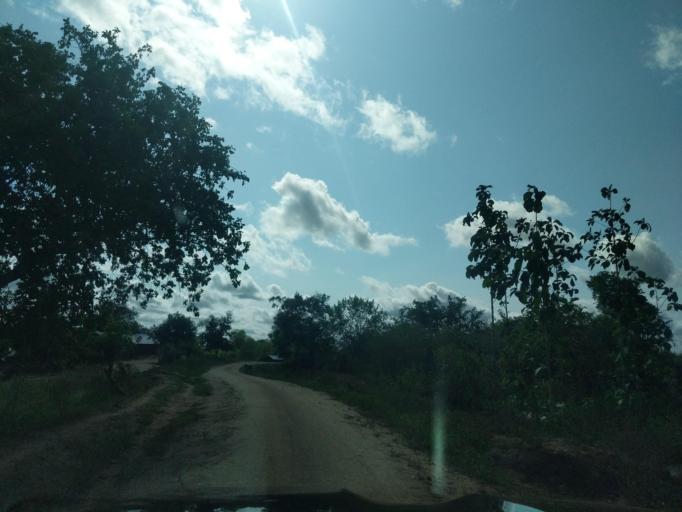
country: TZ
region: Tanga
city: Muheza
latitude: -5.4191
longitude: 38.6456
